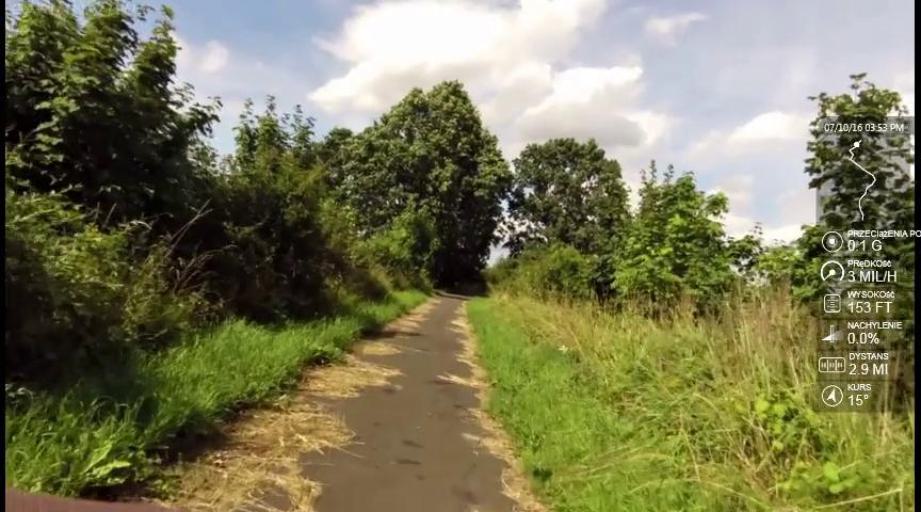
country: PL
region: West Pomeranian Voivodeship
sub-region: Powiat gryfinski
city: Banie
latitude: 53.1478
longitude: 14.6232
